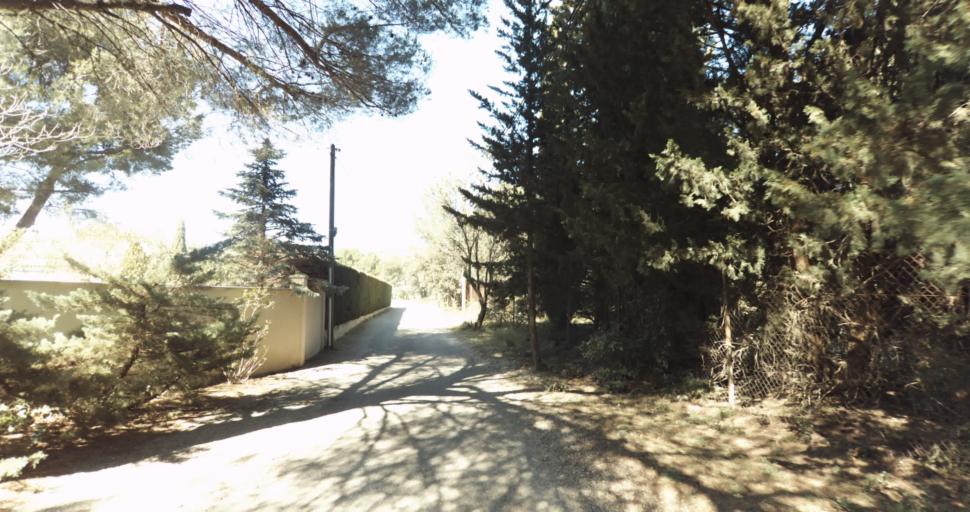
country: FR
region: Provence-Alpes-Cote d'Azur
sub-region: Departement des Bouches-du-Rhone
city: Pelissanne
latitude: 43.6418
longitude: 5.1589
